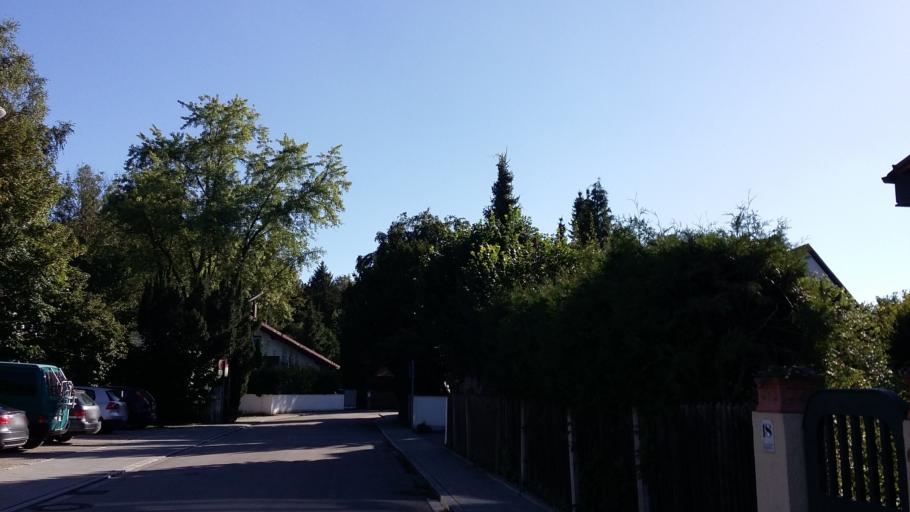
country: DE
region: Bavaria
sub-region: Upper Bavaria
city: Krailling
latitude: 48.0899
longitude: 11.4026
